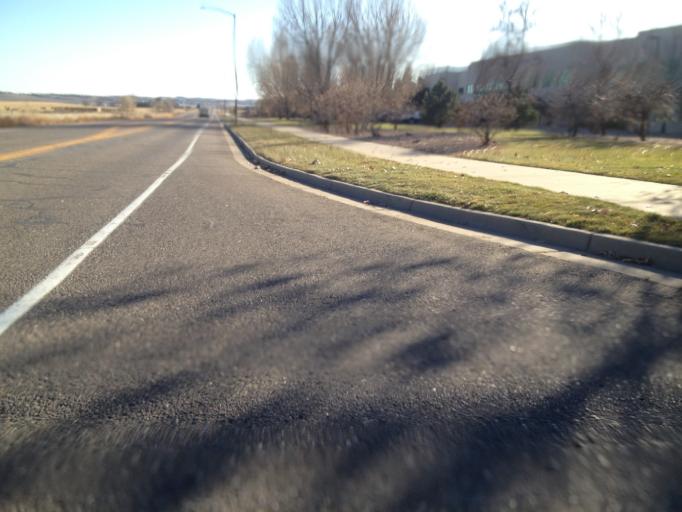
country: US
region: Colorado
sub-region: Boulder County
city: Louisville
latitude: 39.9674
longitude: -105.1094
